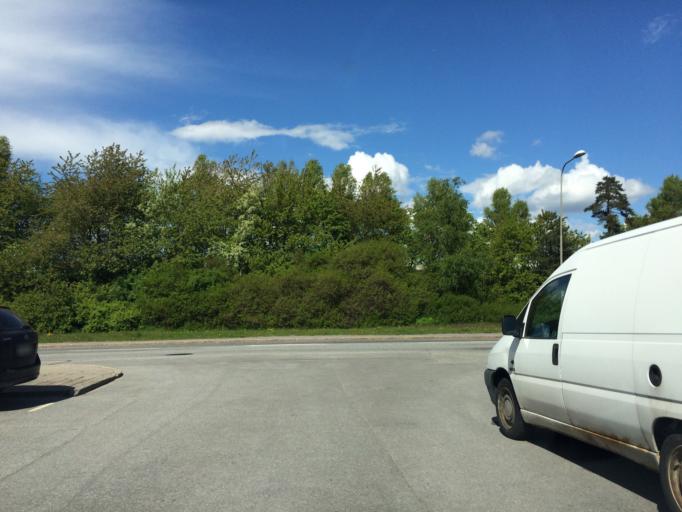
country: SE
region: Stockholm
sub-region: Huddinge Kommun
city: Segeltorp
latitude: 59.2884
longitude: 17.9705
